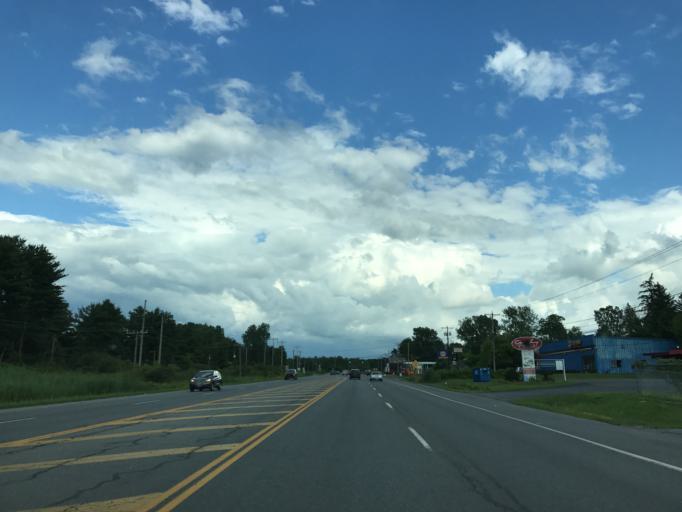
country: US
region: New York
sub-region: Warren County
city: Glens Falls
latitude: 43.3313
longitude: -73.6398
